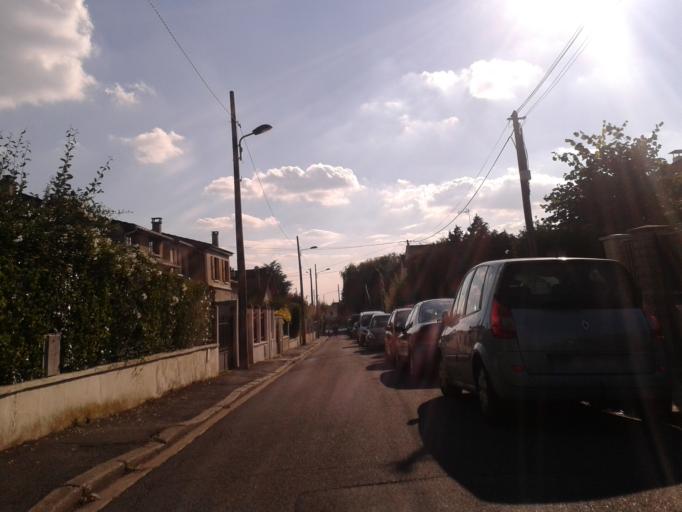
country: FR
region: Ile-de-France
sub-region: Departement du Val-d'Oise
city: La Frette-sur-Seine
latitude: 48.9884
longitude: 2.1829
